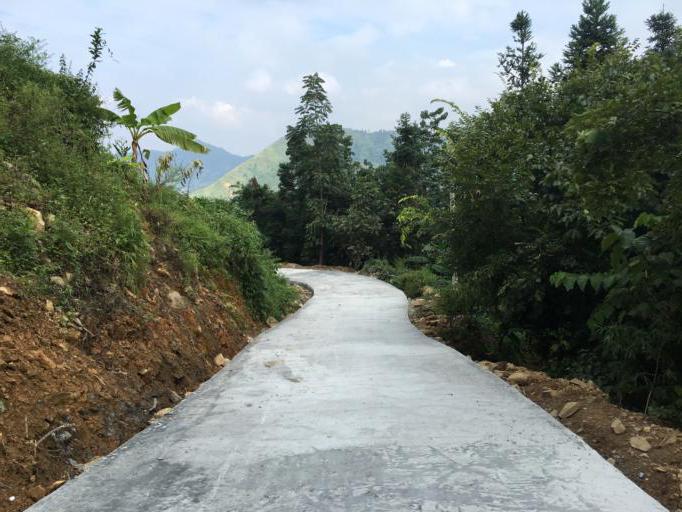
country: CN
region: Guangxi Zhuangzu Zizhiqu
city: Tongle
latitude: 25.2991
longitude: 106.1643
